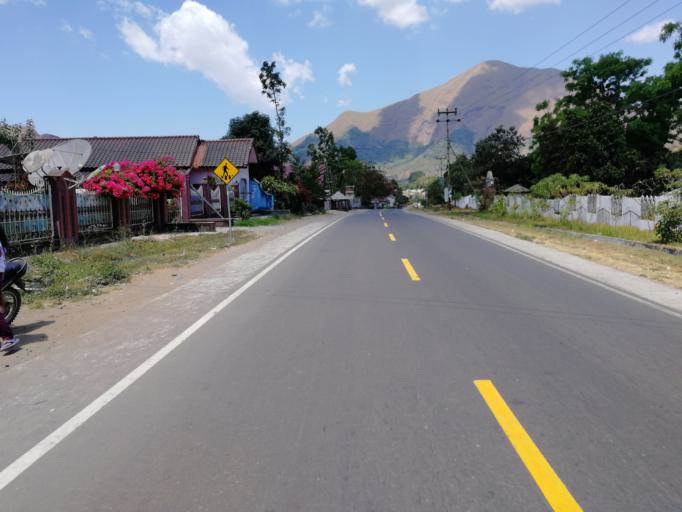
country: ID
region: West Nusa Tenggara
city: Sembalunlawang
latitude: -8.3598
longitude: 116.5281
